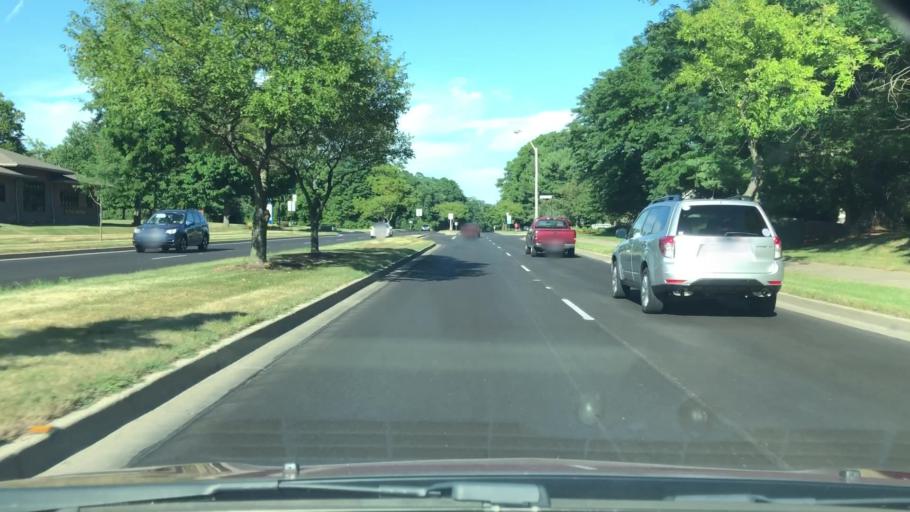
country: US
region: Ohio
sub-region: Montgomery County
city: Centerville
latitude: 39.6486
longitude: -84.1342
